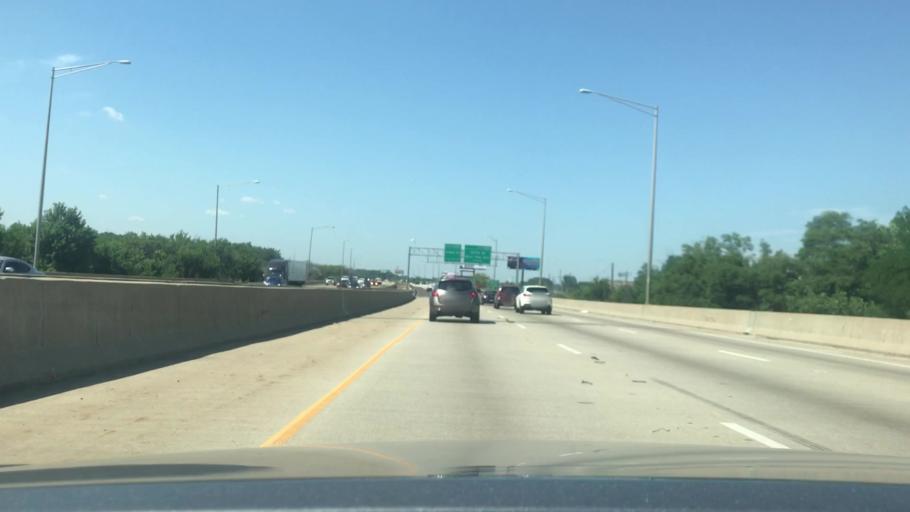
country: US
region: Illinois
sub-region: Cook County
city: Calumet Park
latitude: 41.6517
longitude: -87.6613
